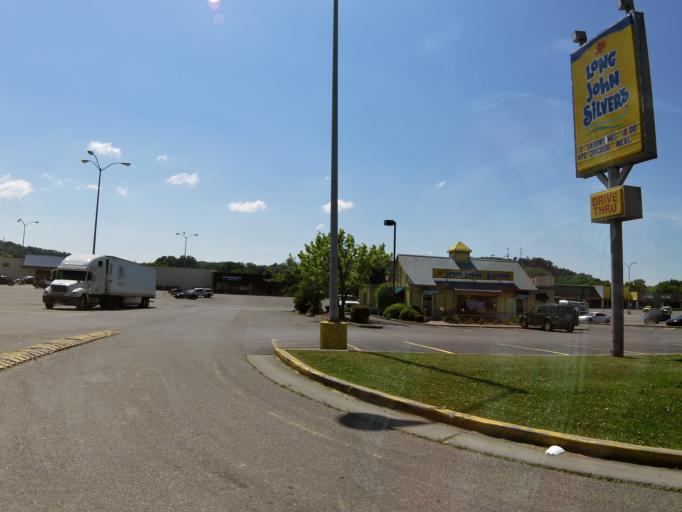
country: US
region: Tennessee
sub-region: Sevier County
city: Sevierville
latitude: 35.8666
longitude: -83.5677
